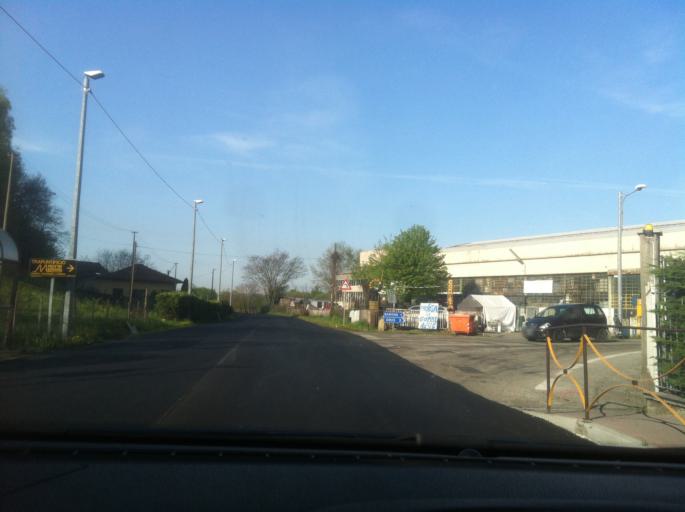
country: IT
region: Piedmont
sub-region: Provincia di Torino
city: Candia Canavese
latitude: 45.3250
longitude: 7.8807
